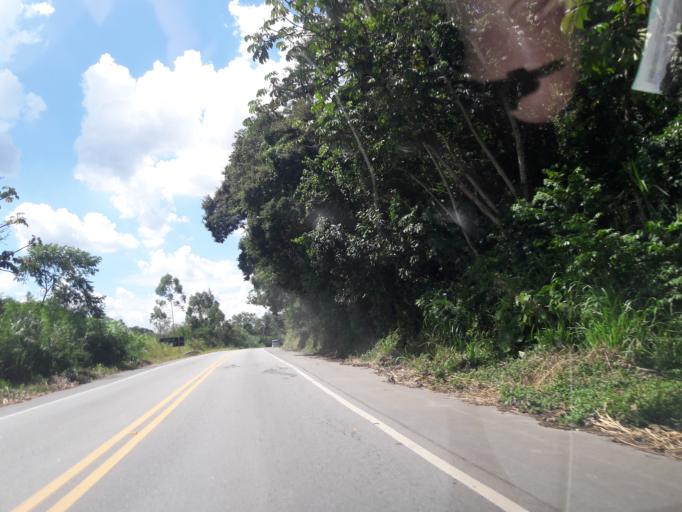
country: BR
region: Sao Paulo
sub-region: Campo Limpo Paulista
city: Campo Limpo Paulista
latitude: -23.2400
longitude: -46.7924
